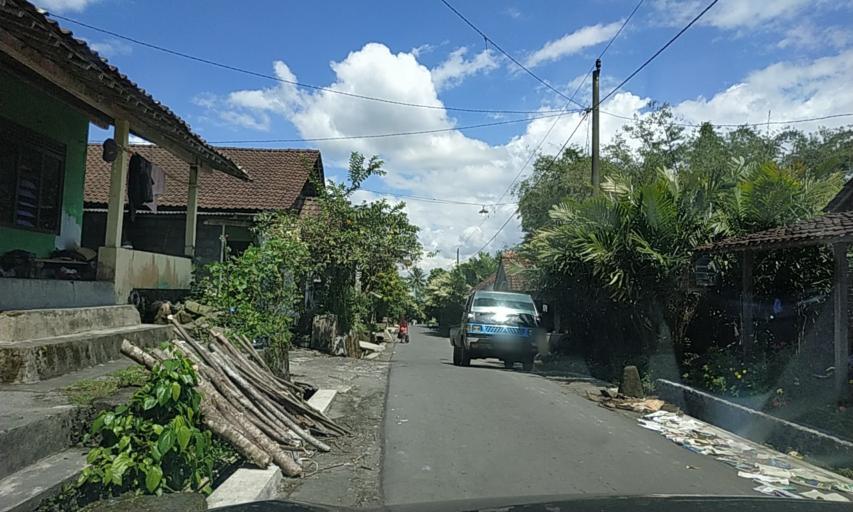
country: ID
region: Central Java
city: Muntilan
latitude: -7.5873
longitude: 110.3557
